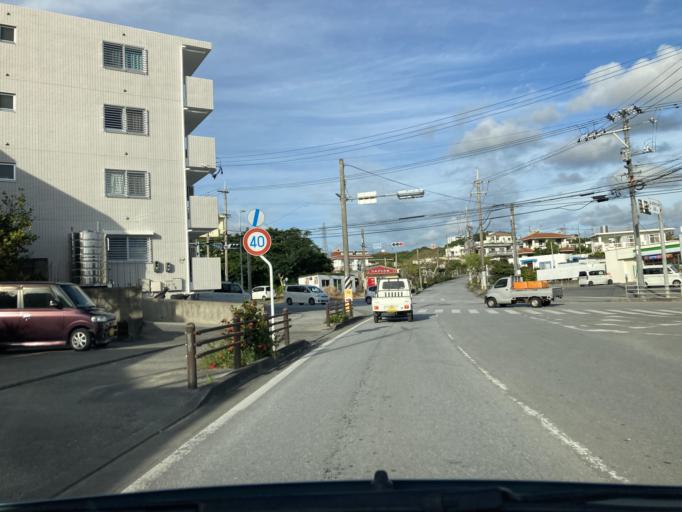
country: JP
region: Okinawa
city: Tomigusuku
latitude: 26.1628
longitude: 127.7395
